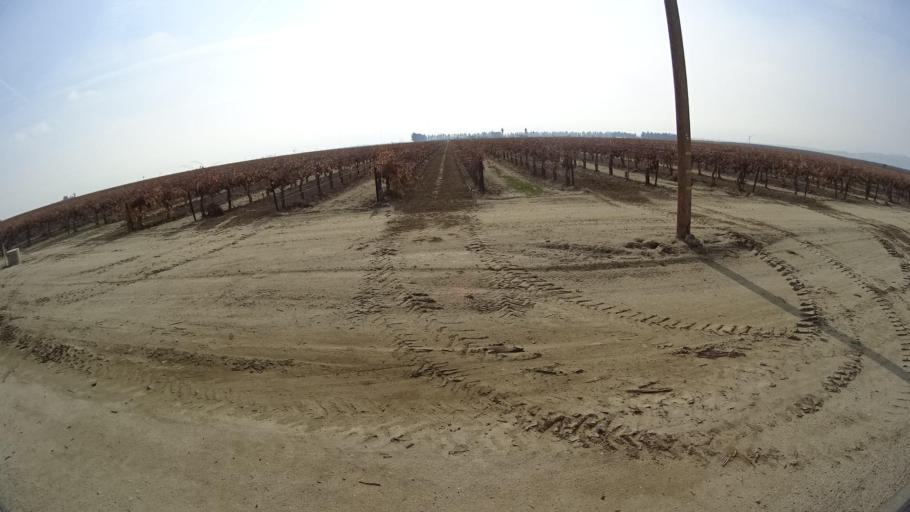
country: US
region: California
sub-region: Kern County
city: Lebec
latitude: 35.0309
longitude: -118.9206
